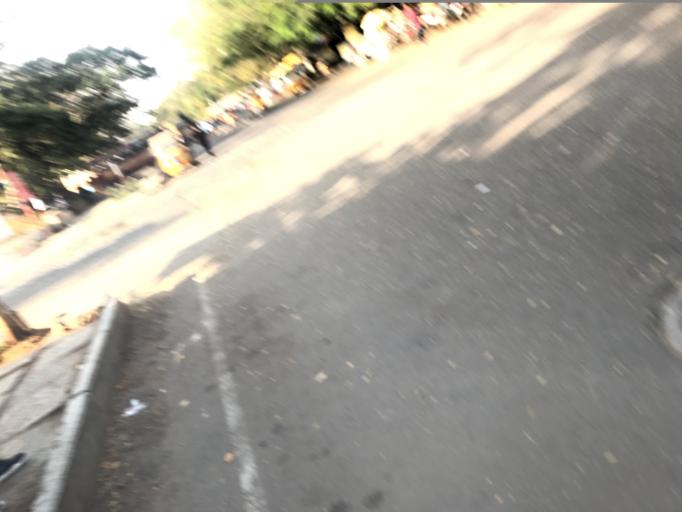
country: IN
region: Tamil Nadu
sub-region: Chennai
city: Chennai
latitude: 13.0793
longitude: 80.2630
